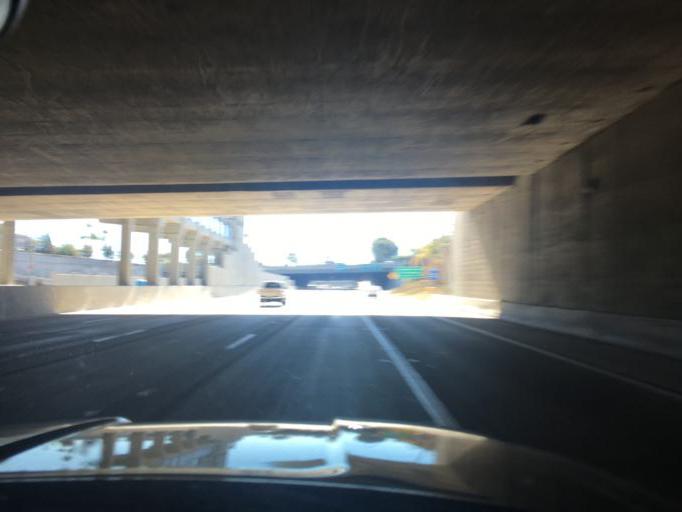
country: US
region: California
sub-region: San Diego County
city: San Diego
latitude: 32.7556
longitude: -117.1091
